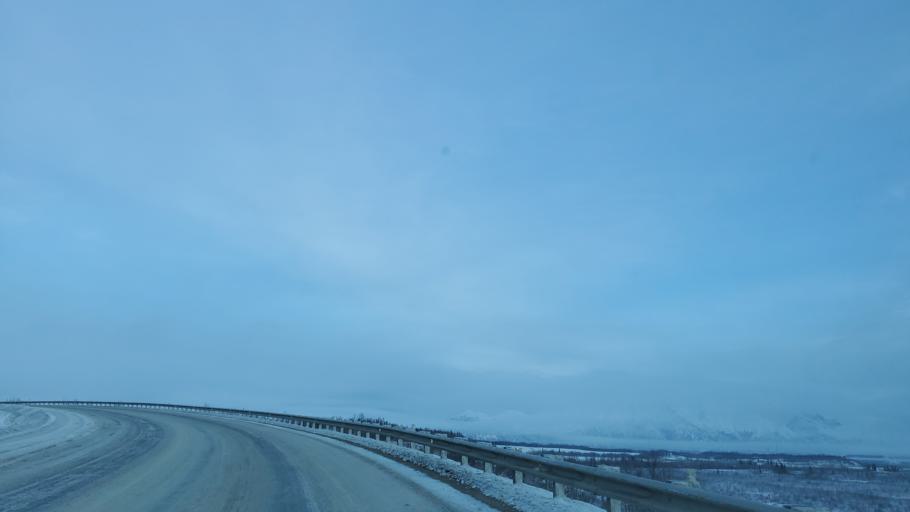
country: US
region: Alaska
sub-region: Matanuska-Susitna Borough
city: Gateway
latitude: 61.5502
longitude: -149.2812
